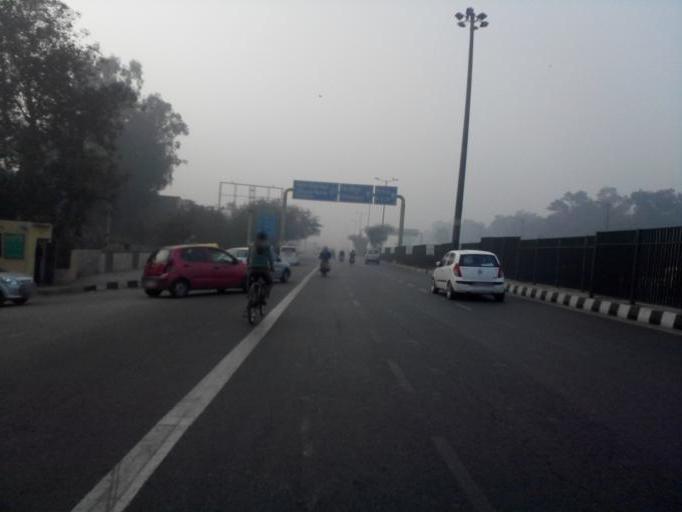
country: IN
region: Uttar Pradesh
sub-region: Gautam Buddha Nagar
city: Noida
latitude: 28.6598
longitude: 77.3201
